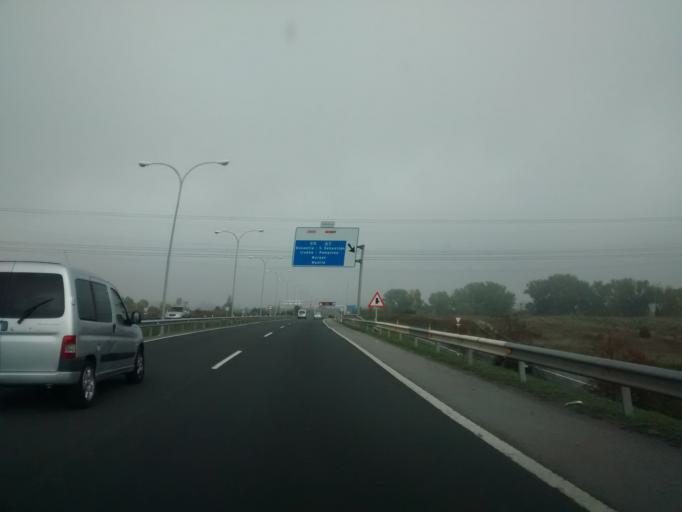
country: ES
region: Basque Country
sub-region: Provincia de Alava
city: Gasteiz / Vitoria
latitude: 42.8731
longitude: -2.6912
